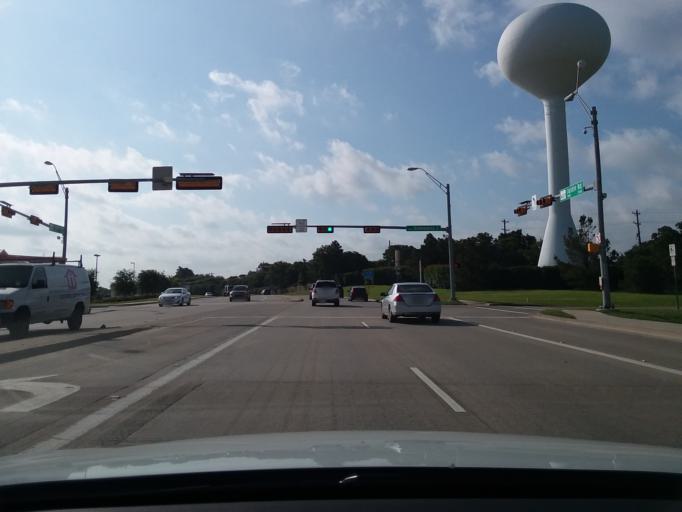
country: US
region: Texas
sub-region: Denton County
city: Double Oak
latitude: 33.0730
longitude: -97.1141
